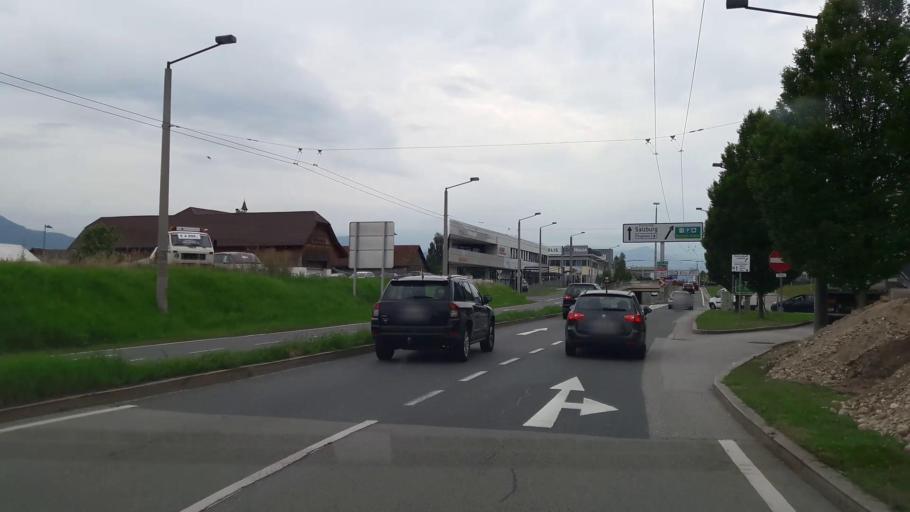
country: DE
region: Bavaria
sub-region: Upper Bavaria
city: Ainring
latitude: 47.7943
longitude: 12.9879
